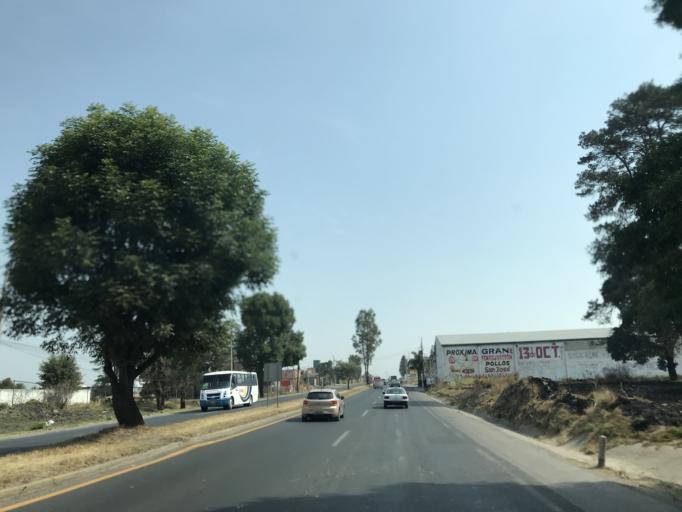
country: MX
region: Tlaxcala
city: Xiloxoxtla
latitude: 19.2614
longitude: -98.1999
